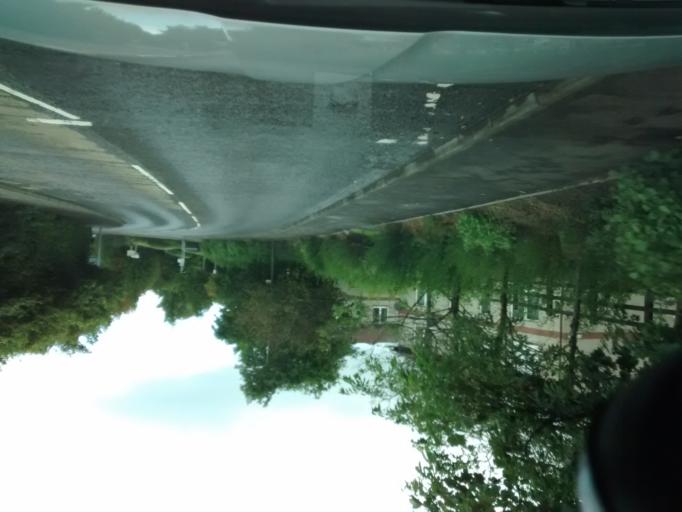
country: GB
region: Scotland
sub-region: West Lothian
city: Bathgate
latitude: 55.9022
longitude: -3.6470
